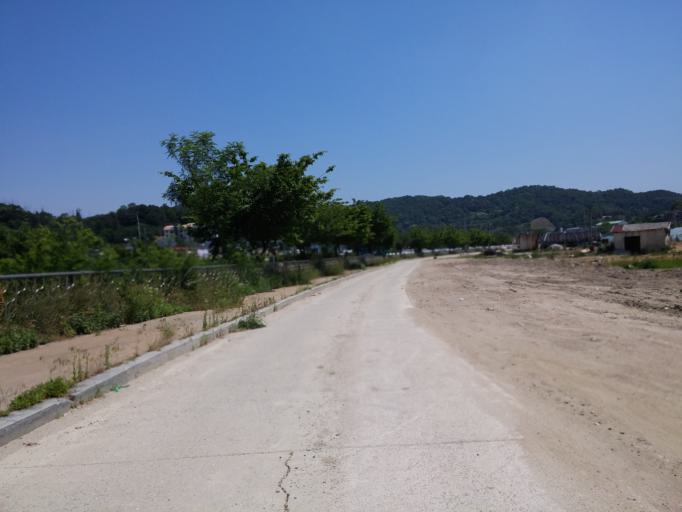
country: KR
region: Chungcheongbuk-do
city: Cheongju-si
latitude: 36.5584
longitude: 127.4342
